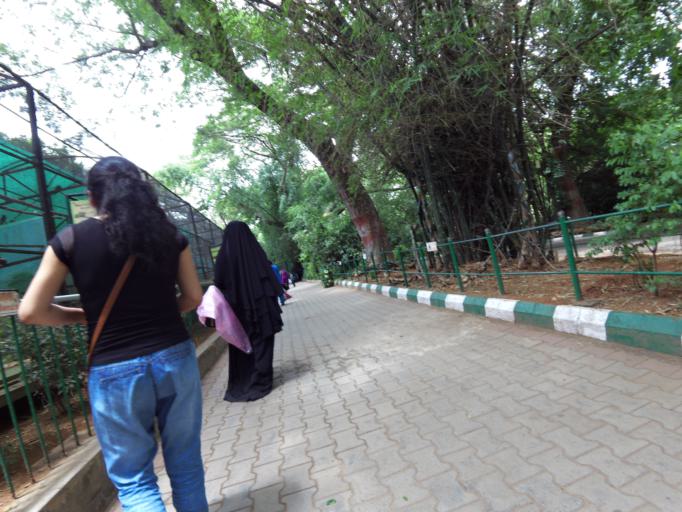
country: IN
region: Karnataka
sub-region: Mysore
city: Mysore
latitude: 12.3029
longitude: 76.6651
